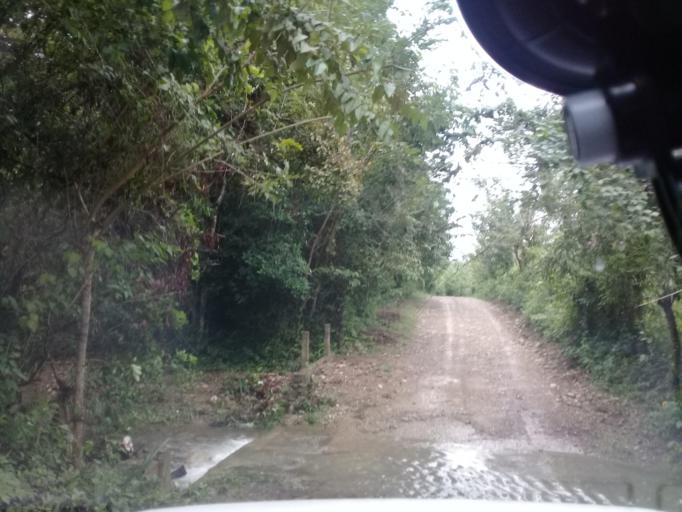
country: MX
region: Veracruz
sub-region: Chalma
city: San Pedro Coyutla
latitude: 21.2398
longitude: -98.4230
